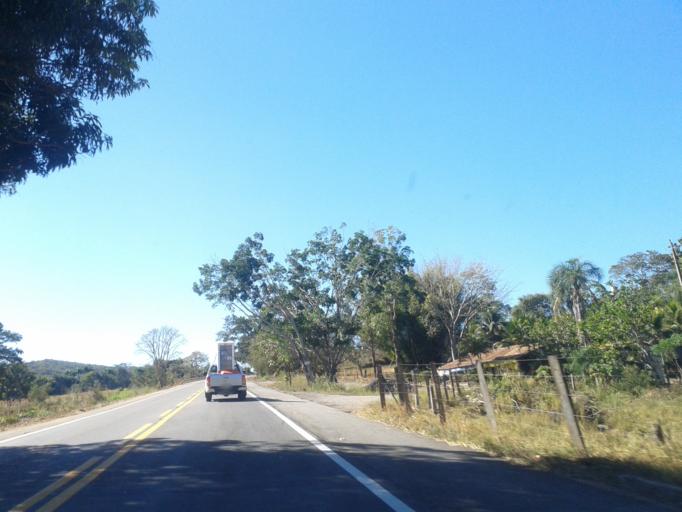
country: BR
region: Goias
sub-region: Goias
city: Goias
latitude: -15.9150
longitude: -50.1270
